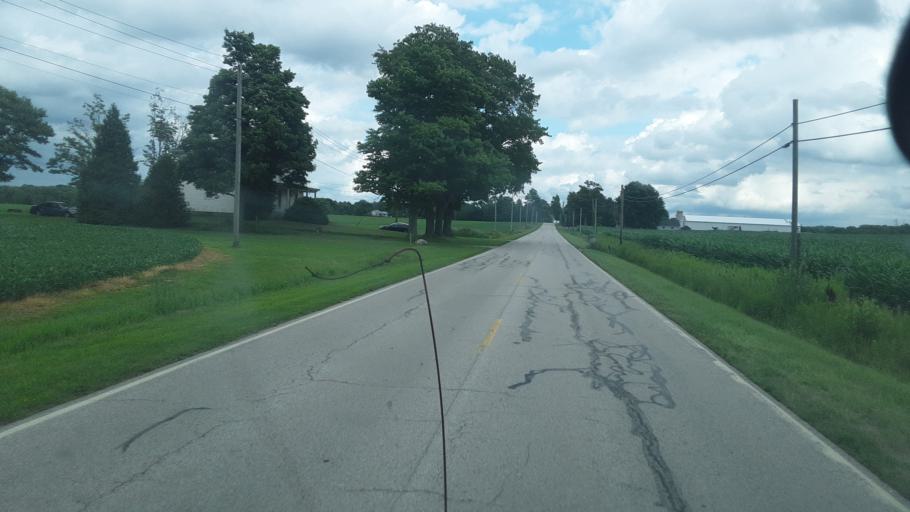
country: US
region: Ohio
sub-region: Ashtabula County
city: Jefferson
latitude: 41.7818
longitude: -80.8272
